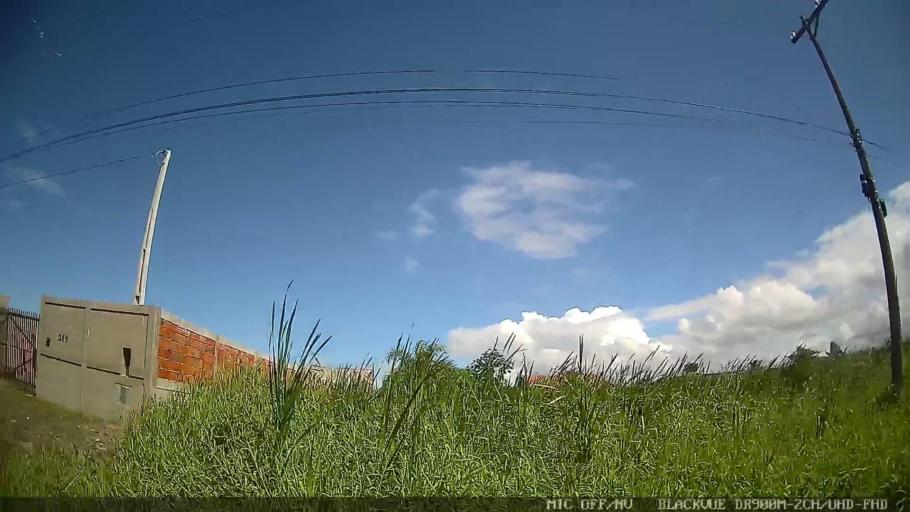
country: BR
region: Sao Paulo
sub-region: Itanhaem
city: Itanhaem
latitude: -24.2258
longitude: -46.8692
